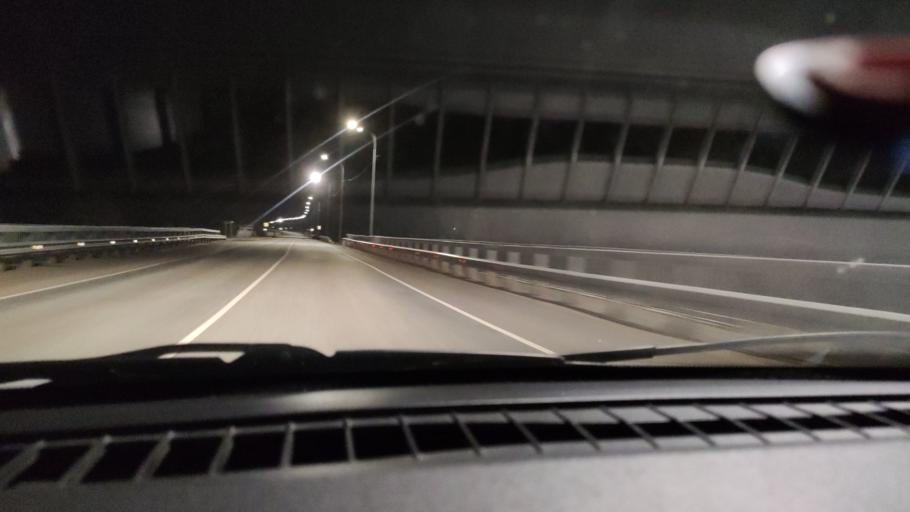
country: RU
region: Bashkortostan
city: Yermolayevo
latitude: 52.5881
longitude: 55.8504
